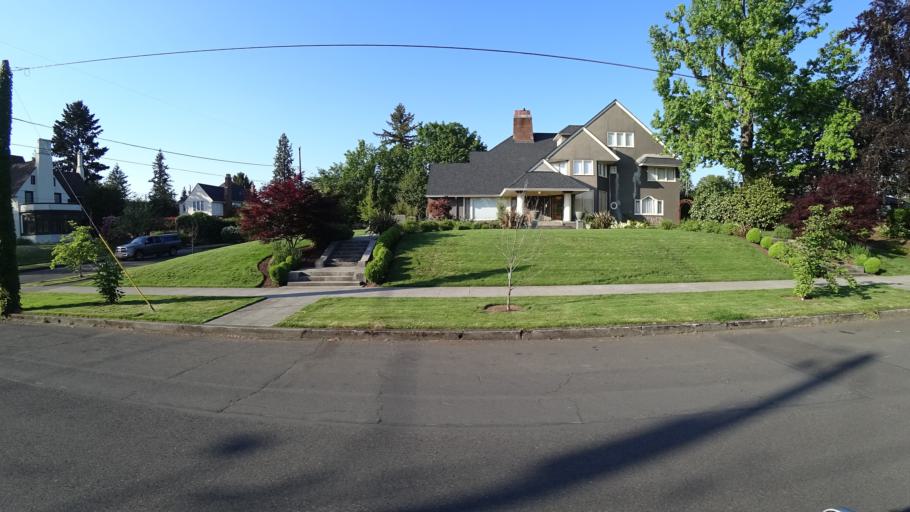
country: US
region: Oregon
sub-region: Multnomah County
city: Portland
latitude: 45.5502
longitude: -122.6380
